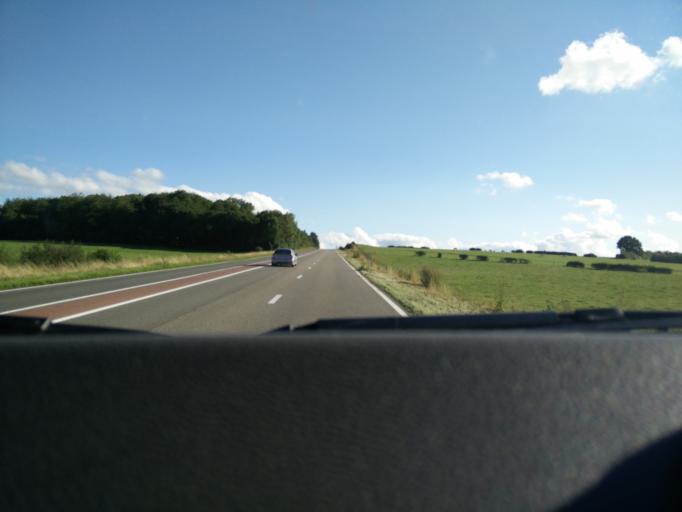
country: BE
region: Wallonia
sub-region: Province du Hainaut
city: Beaumont
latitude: 50.2134
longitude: 4.2262
